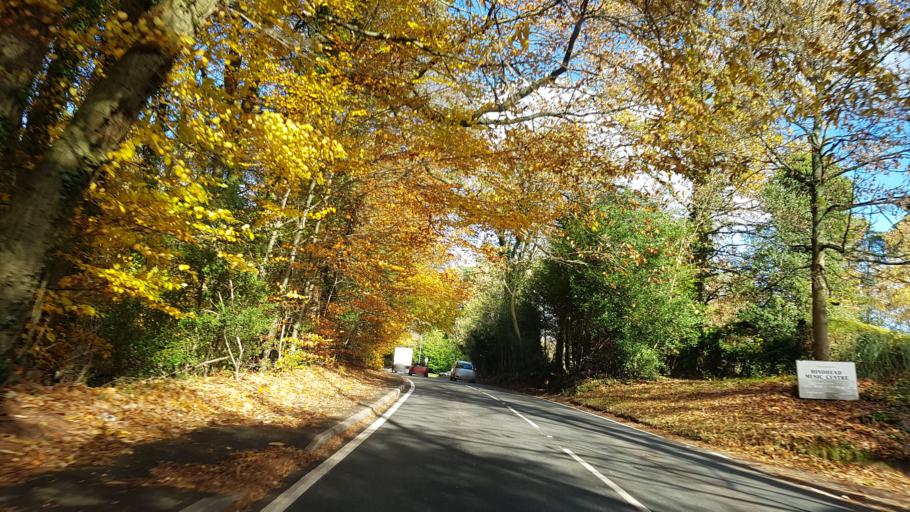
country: GB
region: England
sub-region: Surrey
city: Hindhead
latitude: 51.1024
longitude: -0.7355
